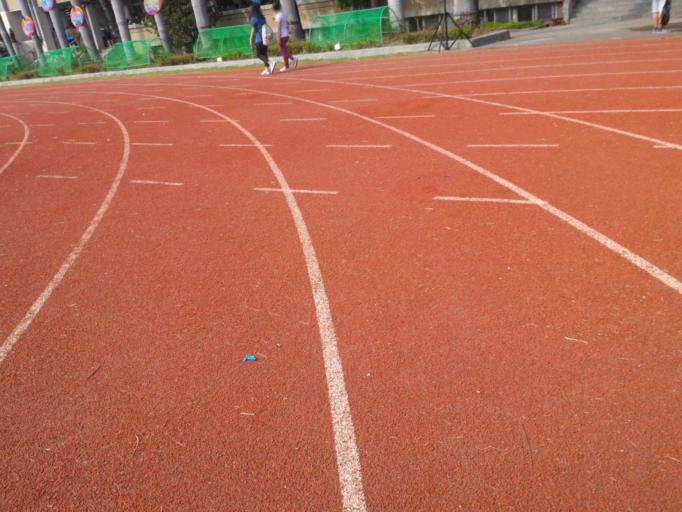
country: TW
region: Taipei
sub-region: Taipei
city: Banqiao
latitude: 25.0282
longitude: 121.4976
